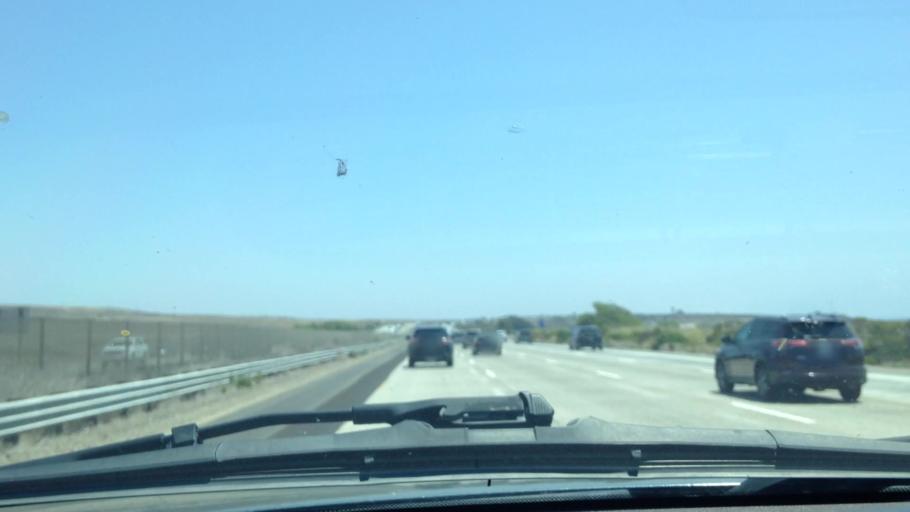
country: US
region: California
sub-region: San Diego County
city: Camp Pendleton South
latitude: 33.3286
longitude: -117.4927
